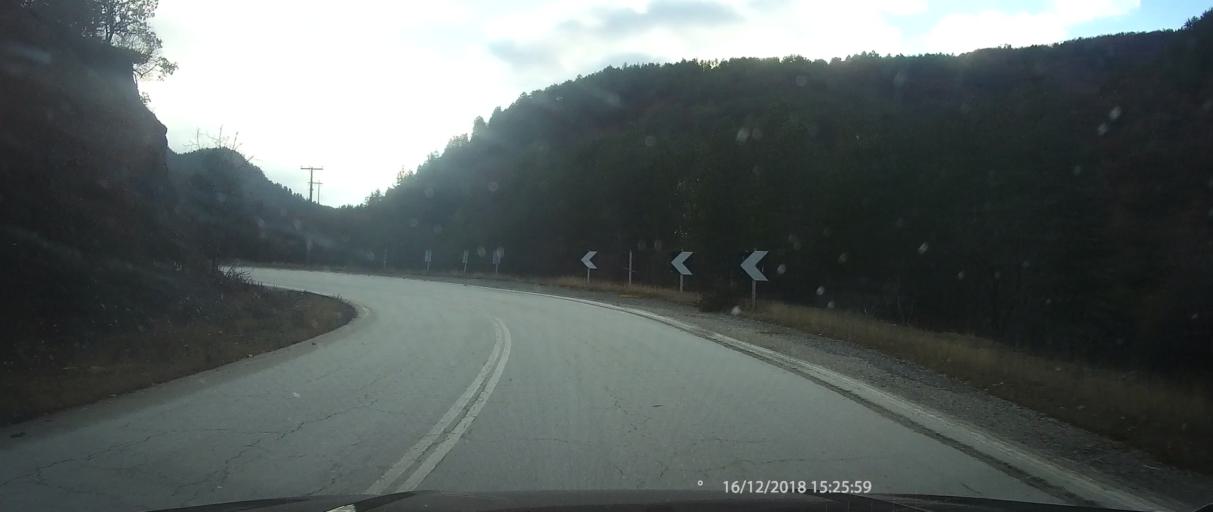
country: GR
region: Epirus
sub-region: Nomos Ioanninon
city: Konitsa
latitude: 40.1217
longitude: 20.7811
